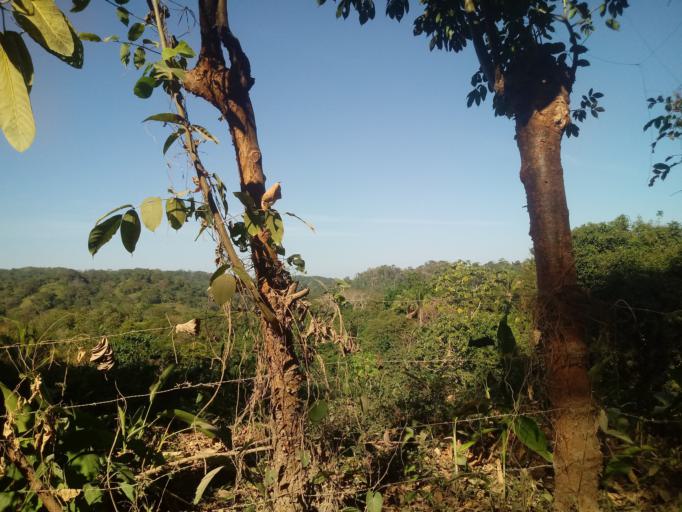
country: CR
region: Puntarenas
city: Paquera
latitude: 9.6074
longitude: -85.1002
